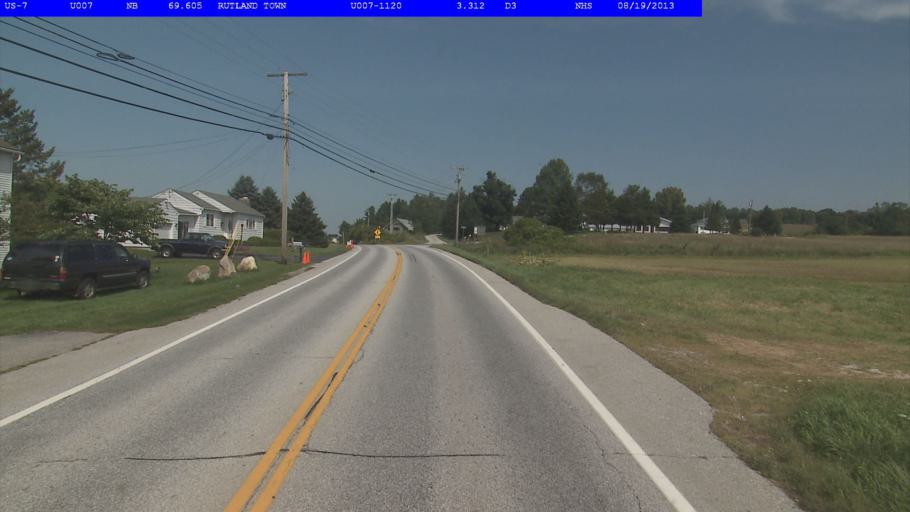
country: US
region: Vermont
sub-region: Rutland County
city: Rutland
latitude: 43.6582
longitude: -72.9881
